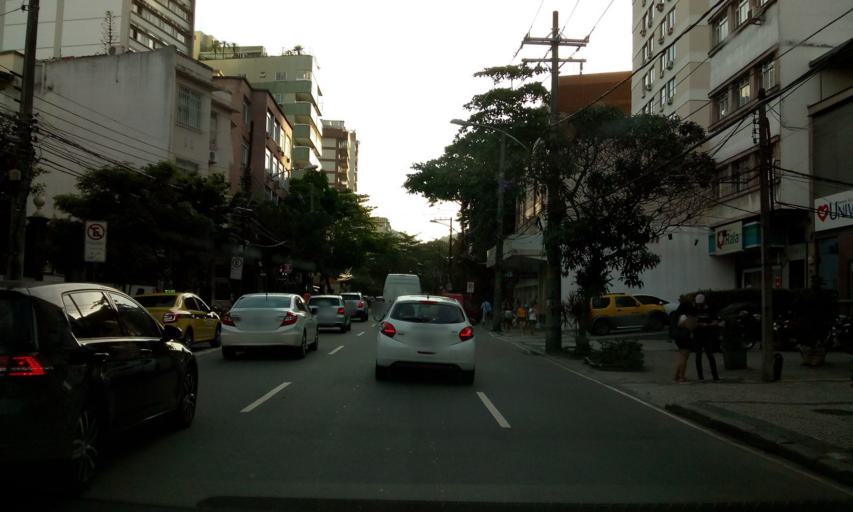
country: BR
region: Rio de Janeiro
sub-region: Rio De Janeiro
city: Rio de Janeiro
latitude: -22.9751
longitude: -43.2271
